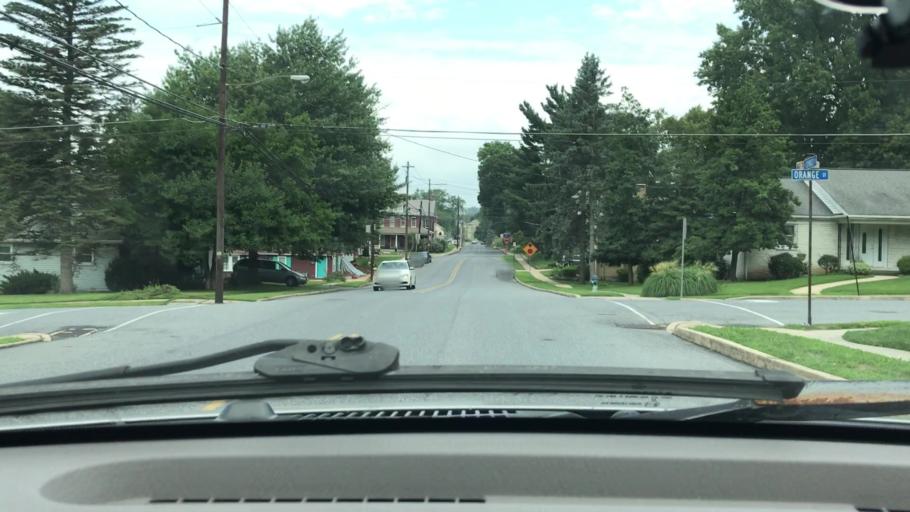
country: US
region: Pennsylvania
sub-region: Lancaster County
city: Elizabethtown
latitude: 40.1474
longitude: -76.5986
